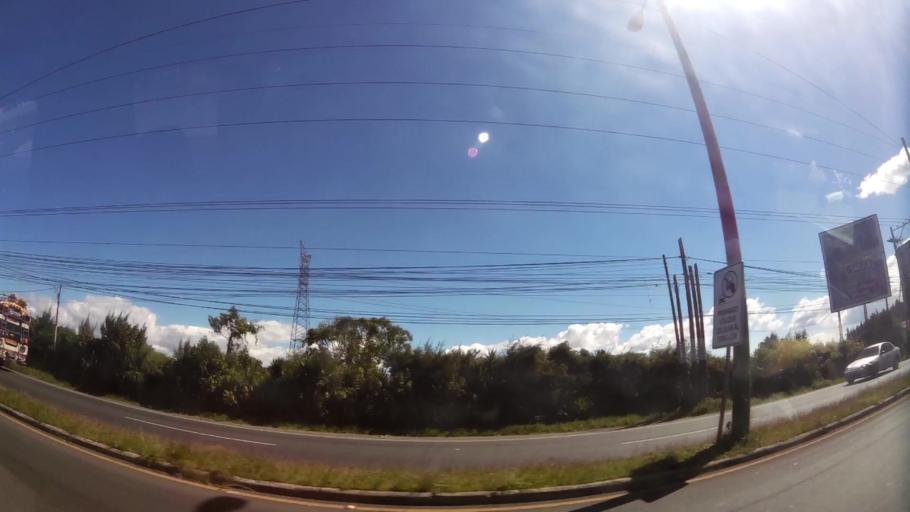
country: GT
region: Guatemala
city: Santa Catarina Pinula
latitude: 14.5142
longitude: -90.4752
